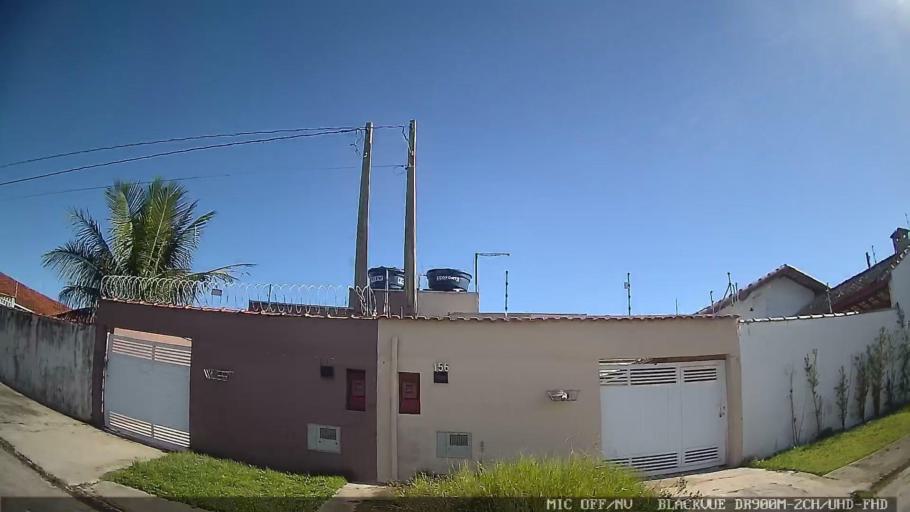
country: BR
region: Sao Paulo
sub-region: Itanhaem
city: Itanhaem
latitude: -24.2091
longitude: -46.8482
